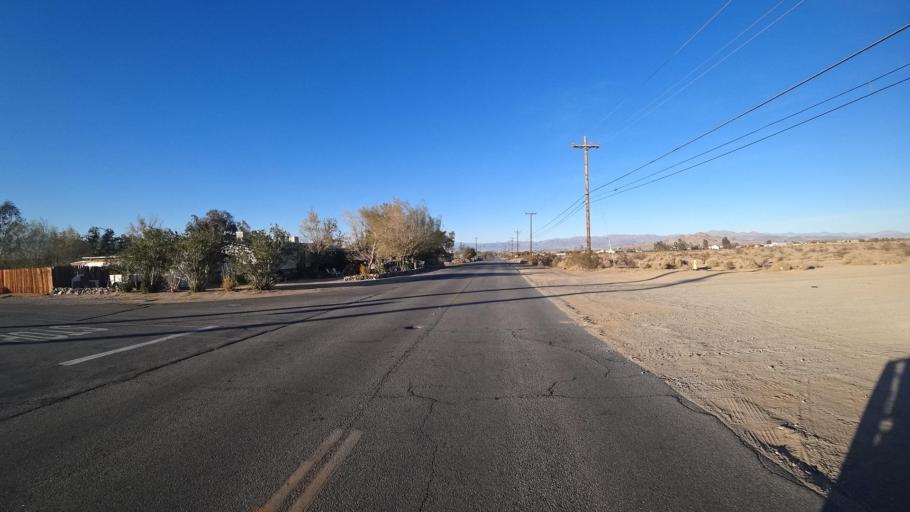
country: US
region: California
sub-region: Kern County
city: Ridgecrest
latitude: 35.5931
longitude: -117.6529
